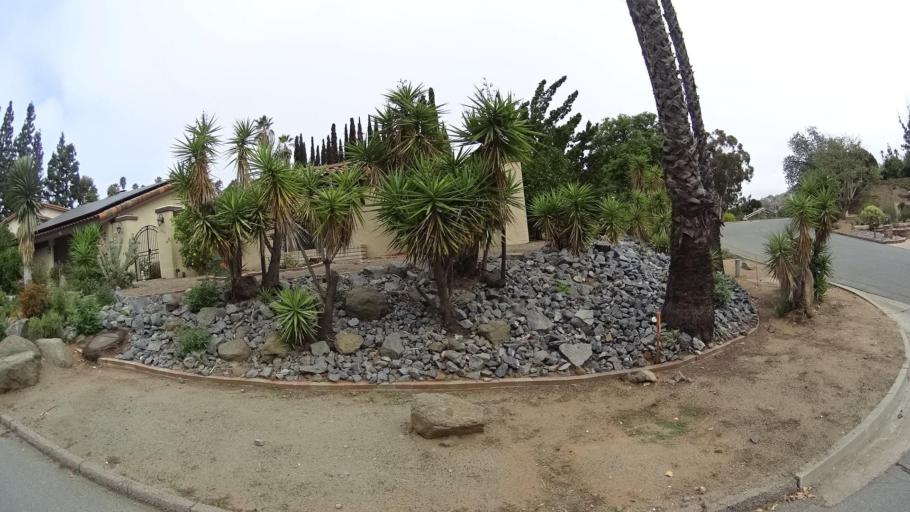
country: US
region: California
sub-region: San Diego County
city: Granite Hills
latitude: 32.7743
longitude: -116.9179
